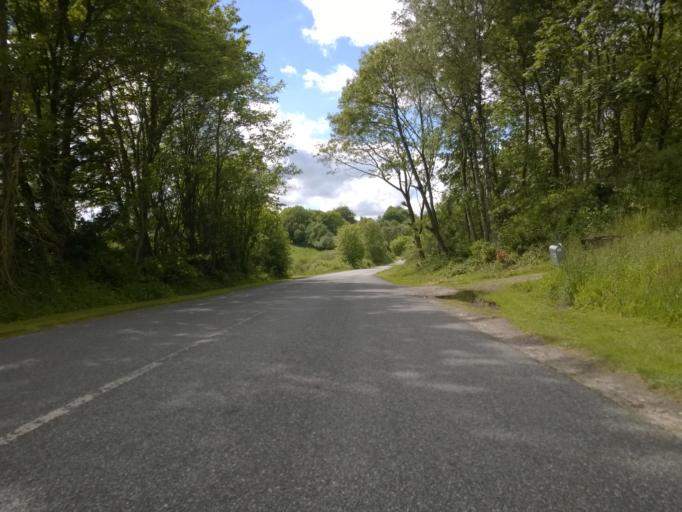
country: DK
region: Central Jutland
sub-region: Holstebro Kommune
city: Vinderup
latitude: 56.4037
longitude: 8.7617
